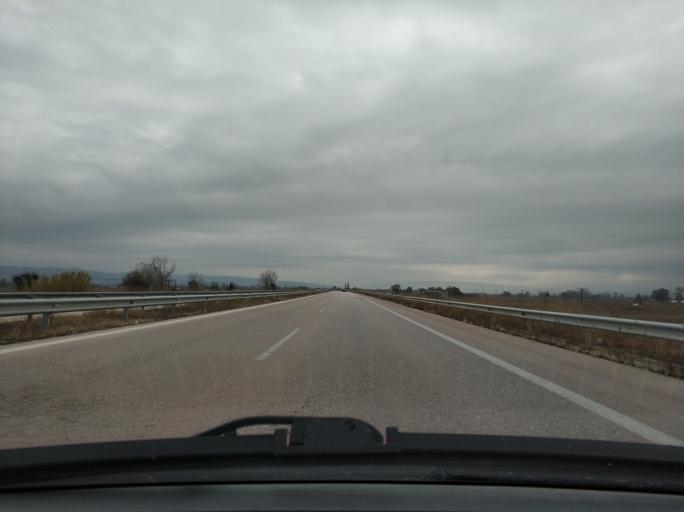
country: GR
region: Central Macedonia
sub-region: Nomos Thessalonikis
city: Lagkadas
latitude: 40.7274
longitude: 23.0705
